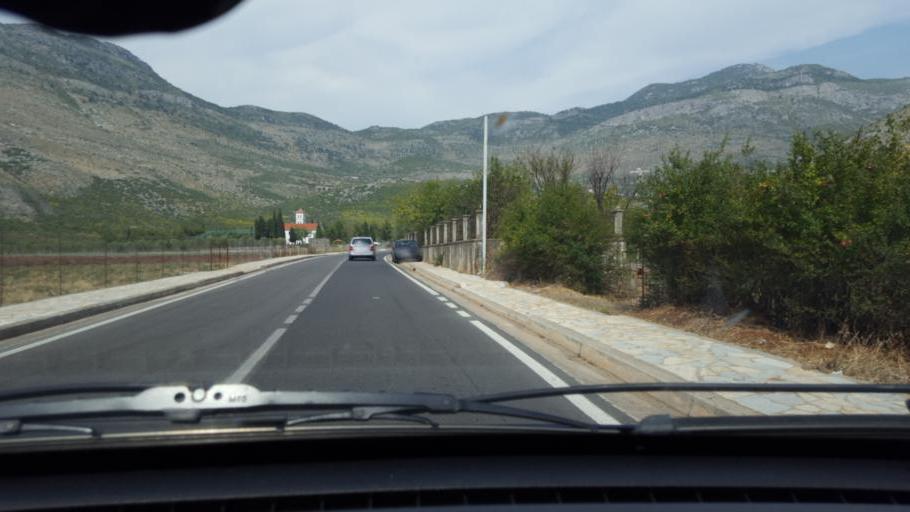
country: AL
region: Shkoder
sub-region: Rrethi i Malesia e Madhe
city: Hot
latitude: 42.3569
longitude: 19.4430
